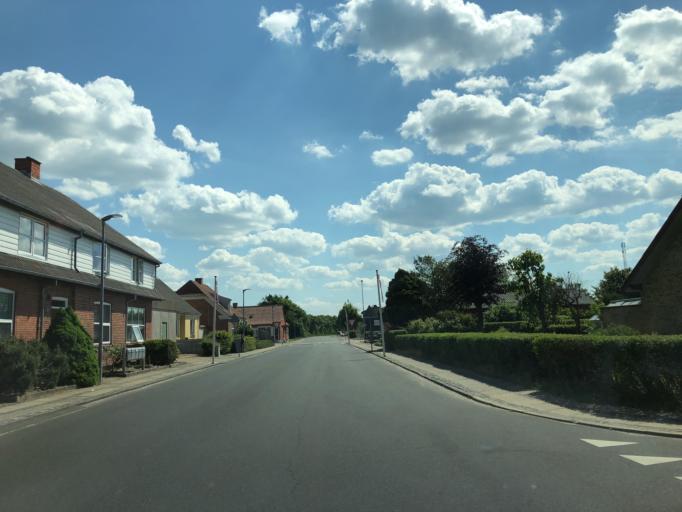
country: DK
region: Central Jutland
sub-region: Holstebro Kommune
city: Ulfborg
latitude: 56.3669
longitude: 8.4289
